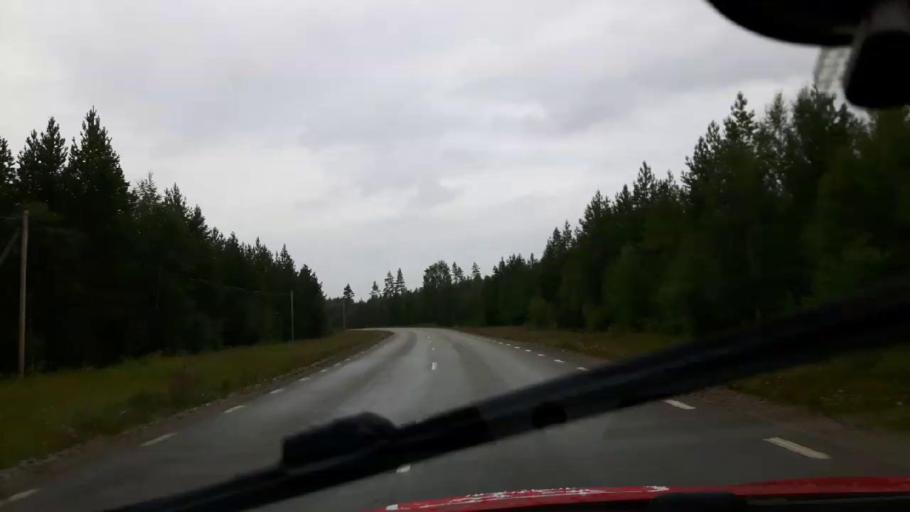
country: SE
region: Jaemtland
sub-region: OEstersunds Kommun
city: Brunflo
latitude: 62.8408
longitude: 15.0085
